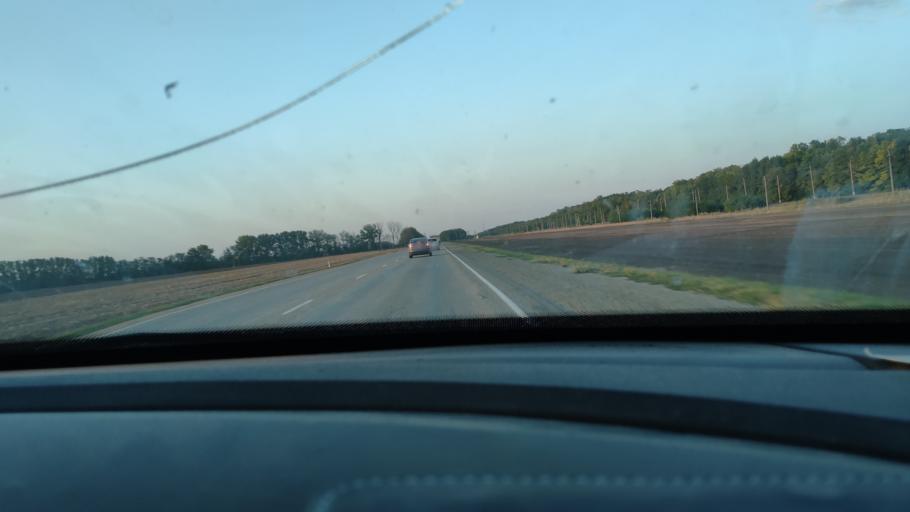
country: RU
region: Krasnodarskiy
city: Starominskaya
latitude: 46.4726
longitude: 39.0457
